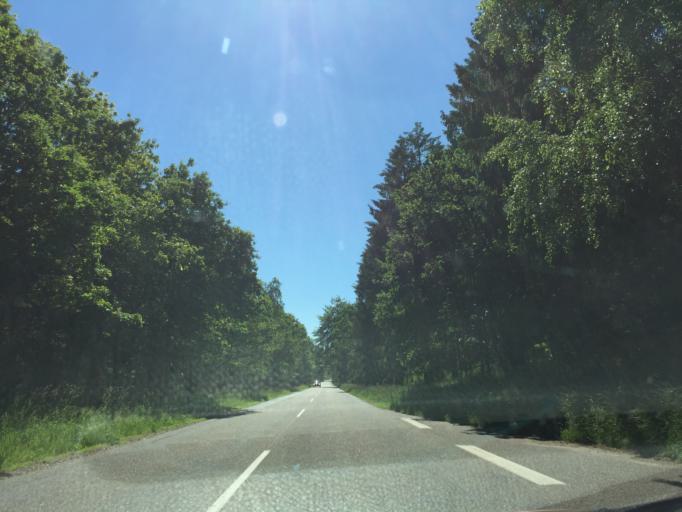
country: DK
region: Central Jutland
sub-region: Viborg Kommune
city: Bjerringbro
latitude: 56.3151
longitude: 9.6099
